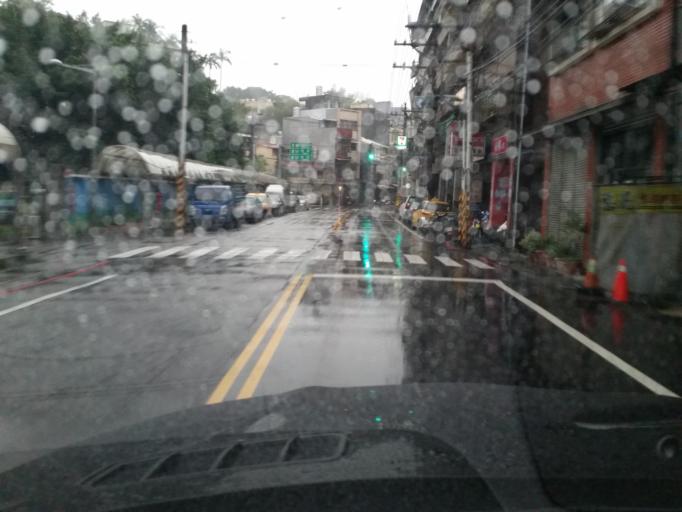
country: TW
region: Taiwan
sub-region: Keelung
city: Keelung
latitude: 25.1451
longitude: 121.7684
